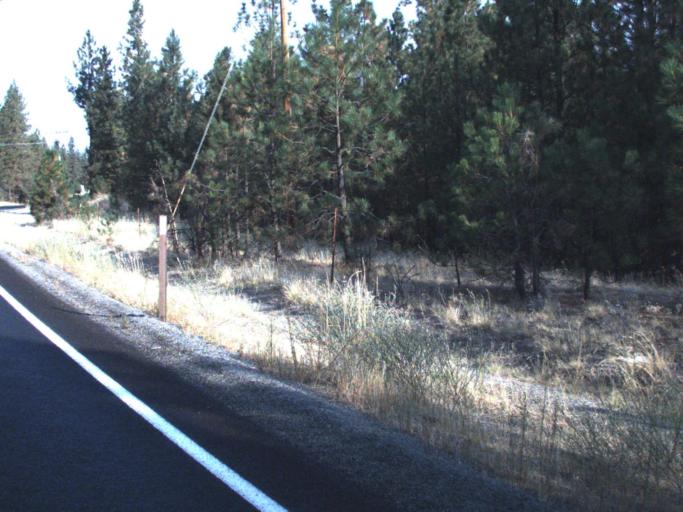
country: US
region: Washington
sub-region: Spokane County
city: Deer Park
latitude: 47.8525
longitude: -117.6410
